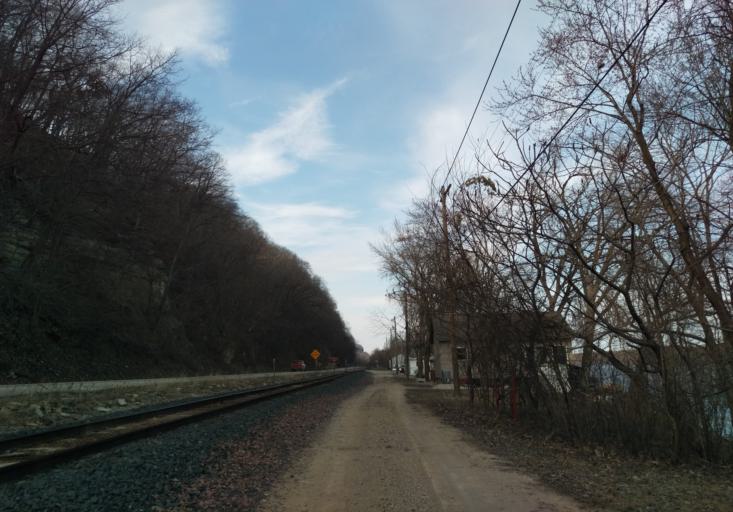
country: US
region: Wisconsin
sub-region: Crawford County
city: Prairie du Chien
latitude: 43.0709
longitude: -91.1802
